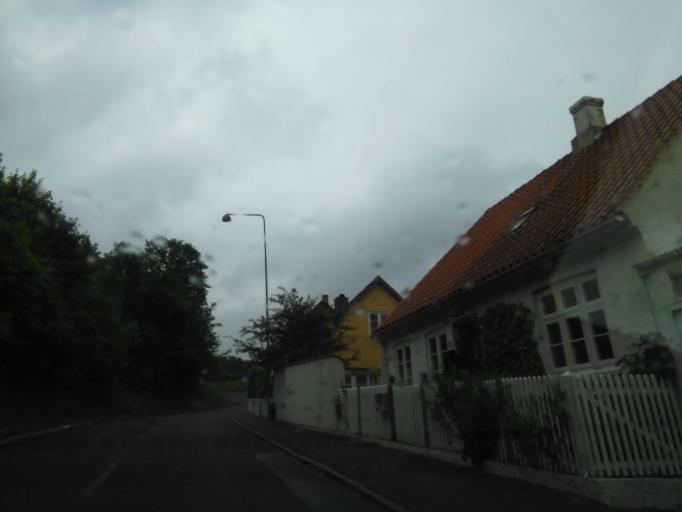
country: DK
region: Capital Region
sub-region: Bornholm Kommune
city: Ronne
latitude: 55.2482
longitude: 14.7381
